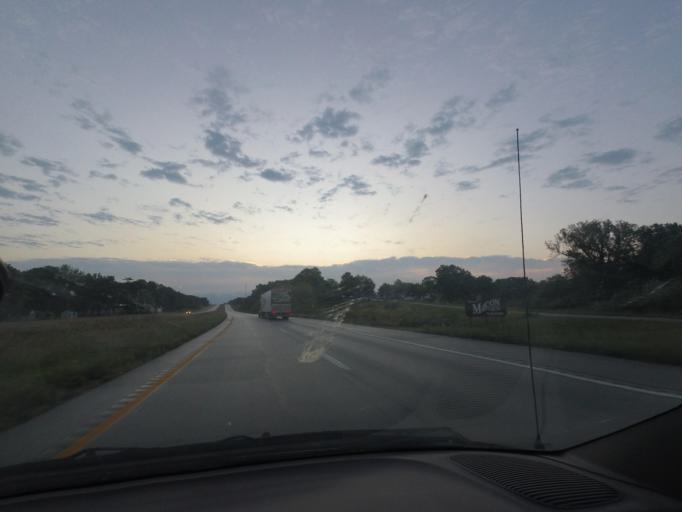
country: US
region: Missouri
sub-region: Macon County
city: Macon
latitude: 39.7465
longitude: -92.4913
